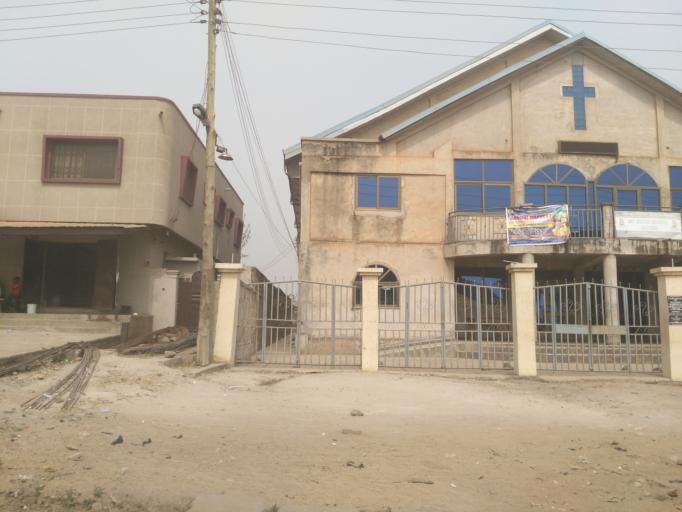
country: GH
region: Ashanti
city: Kumasi
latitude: 6.7016
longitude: -1.5946
